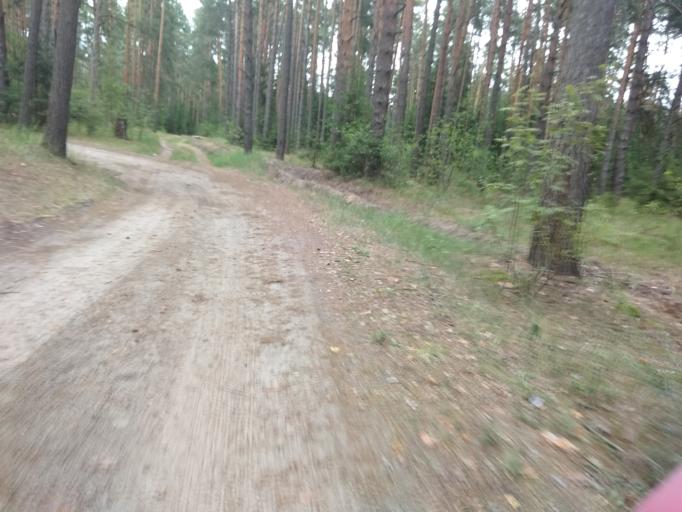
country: RU
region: Moskovskaya
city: Misheronskiy
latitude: 55.6264
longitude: 39.7187
